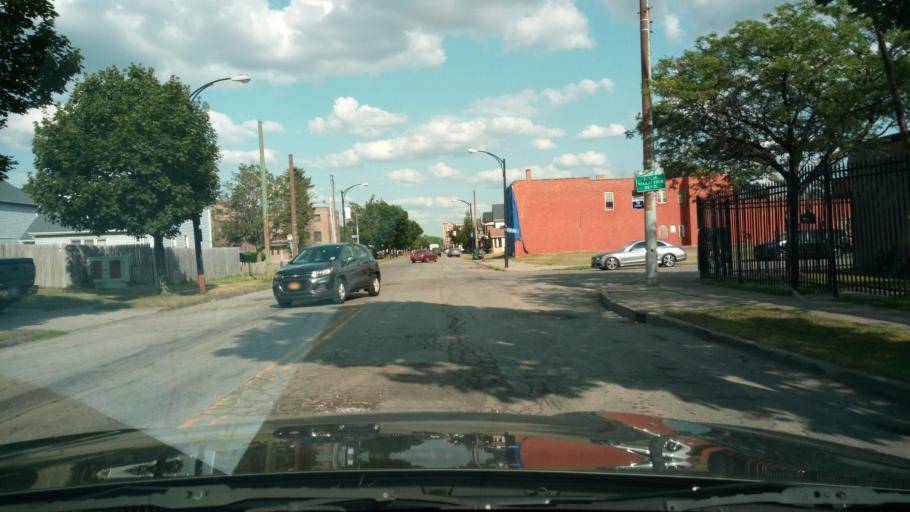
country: US
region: New York
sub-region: Erie County
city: Buffalo
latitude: 42.8802
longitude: -78.8659
